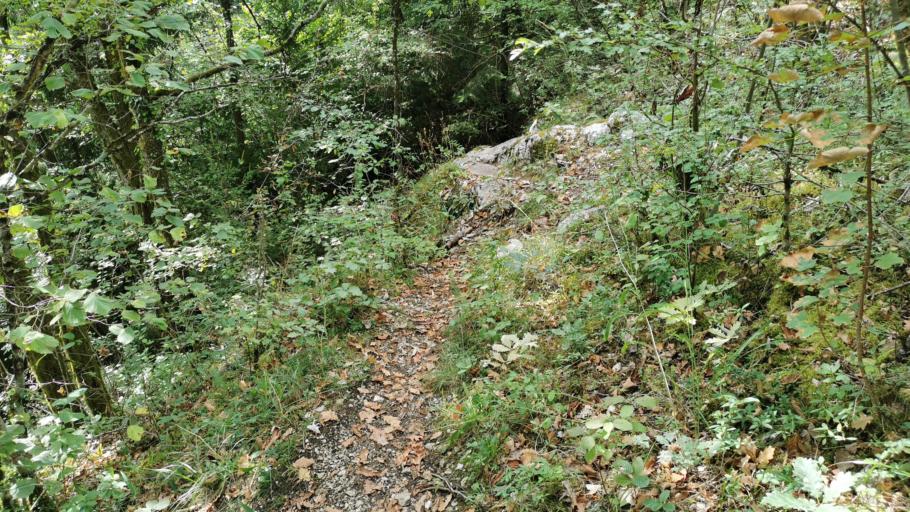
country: FR
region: Rhone-Alpes
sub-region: Departement de la Haute-Savoie
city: Sevrier
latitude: 45.8697
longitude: 6.1358
